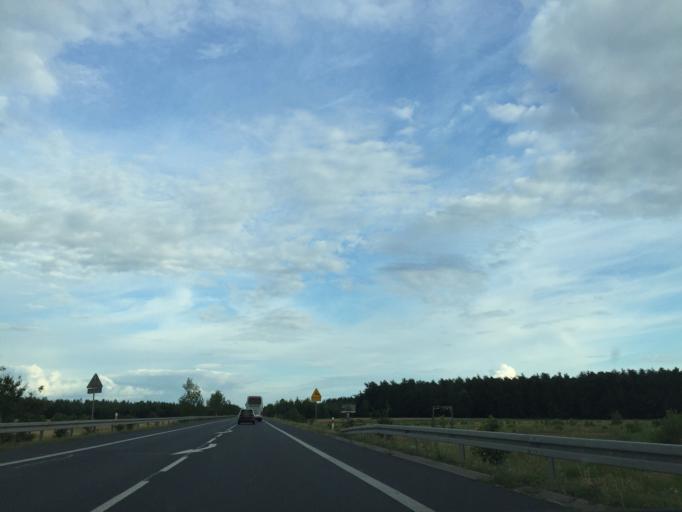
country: PL
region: Lublin Voivodeship
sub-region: Powiat lubartowski
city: Lubartow
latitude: 51.4494
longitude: 22.5809
